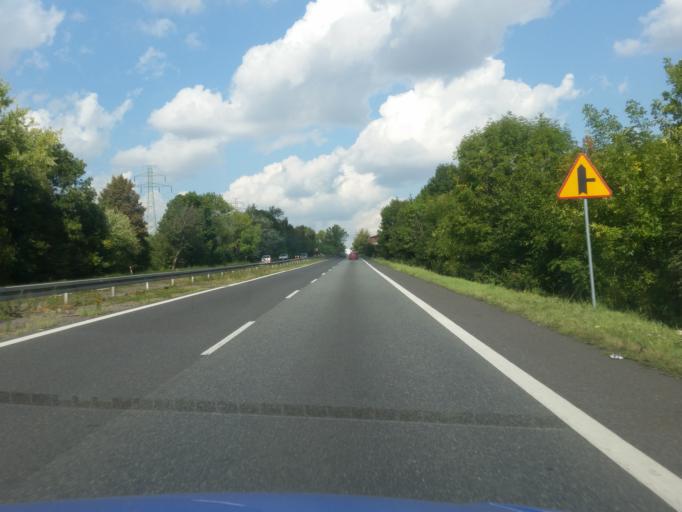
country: PL
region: Silesian Voivodeship
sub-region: Powiat bedzinski
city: Bedzin
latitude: 50.3458
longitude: 19.1103
